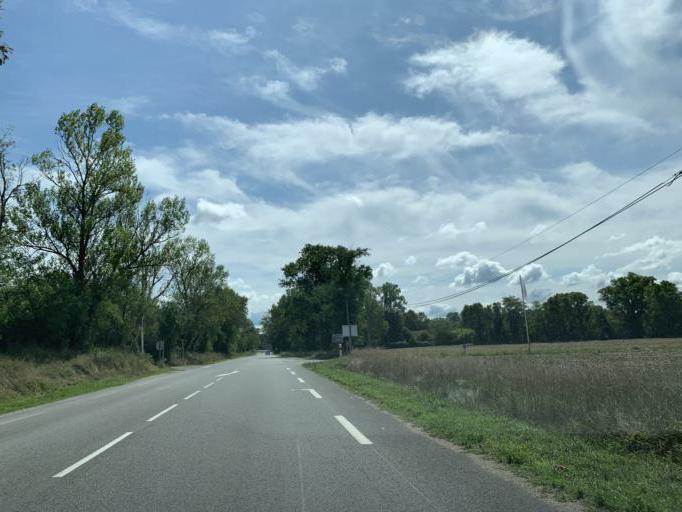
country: FR
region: Rhone-Alpes
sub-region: Departement du Rhone
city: Jons
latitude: 45.8166
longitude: 5.0774
